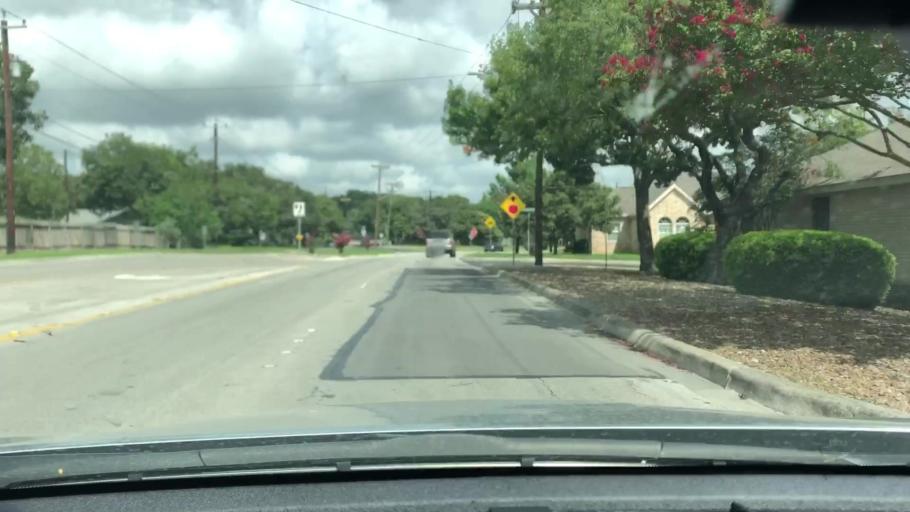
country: US
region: Texas
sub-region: Bexar County
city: Windcrest
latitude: 29.5138
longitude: -98.3716
